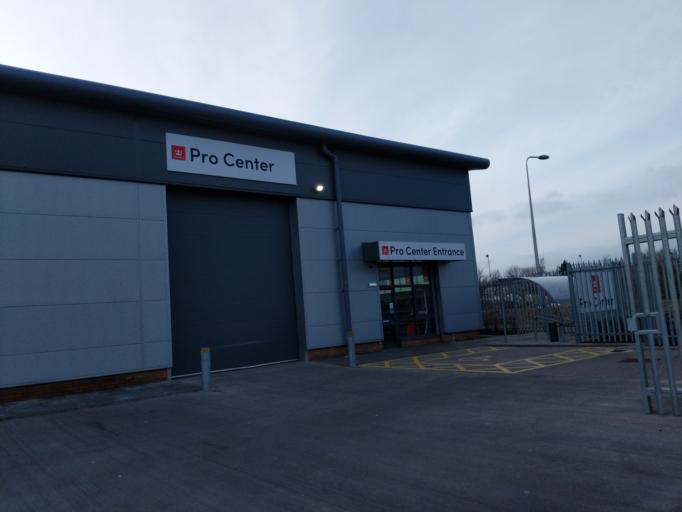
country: GB
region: Scotland
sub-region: Edinburgh
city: Currie
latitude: 55.9289
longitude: -3.3000
